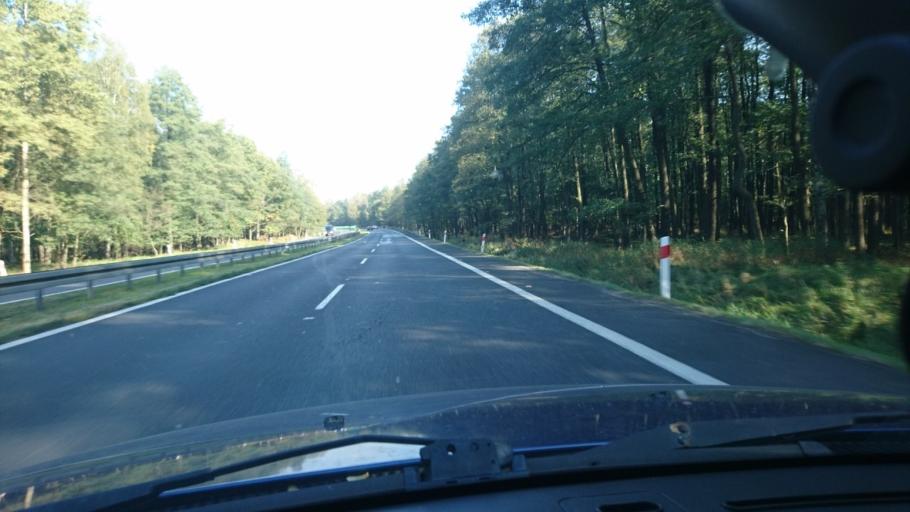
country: PL
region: Silesian Voivodeship
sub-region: Katowice
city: Murcki
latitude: 50.1494
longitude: 19.0238
